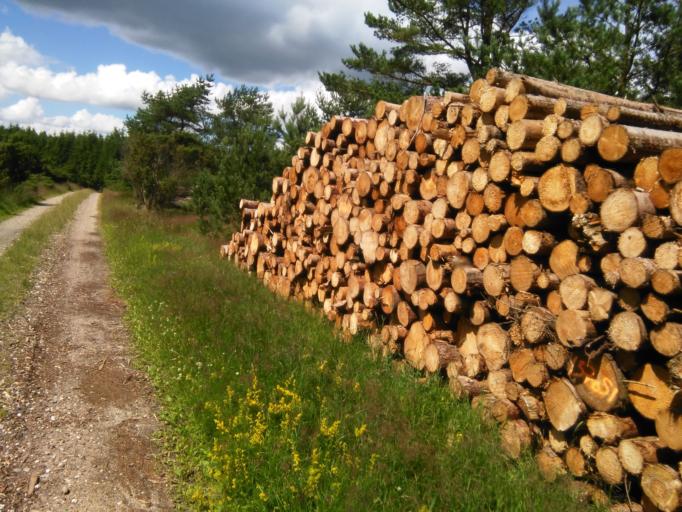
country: DK
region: Central Jutland
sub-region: Silkeborg Kommune
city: Virklund
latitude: 56.0797
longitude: 9.4476
